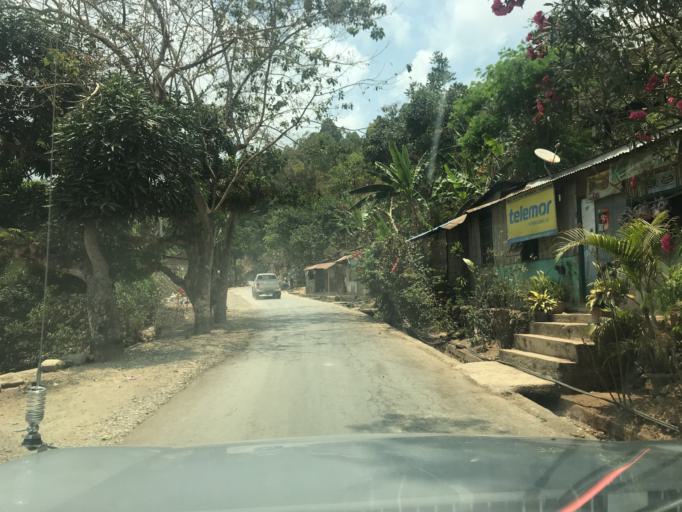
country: TL
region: Dili
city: Dili
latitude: -8.5998
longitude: 125.5914
